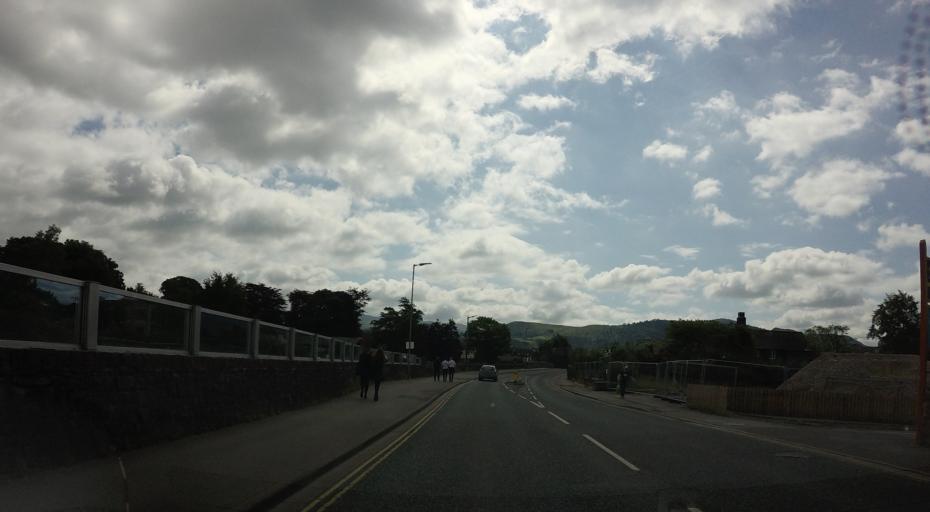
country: GB
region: England
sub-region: Cumbria
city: Keswick
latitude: 54.6042
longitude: -3.1436
